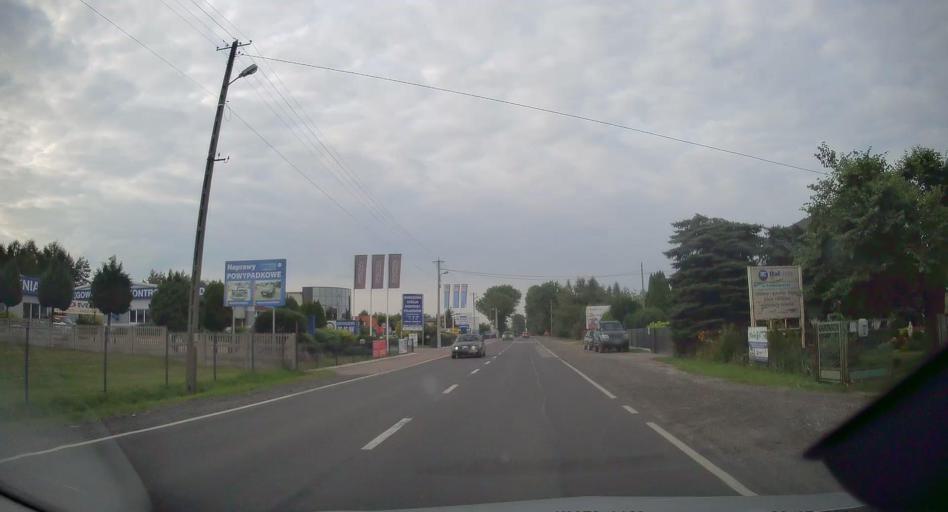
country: PL
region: Lodz Voivodeship
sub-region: Powiat radomszczanski
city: Radomsko
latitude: 51.0995
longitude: 19.4614
